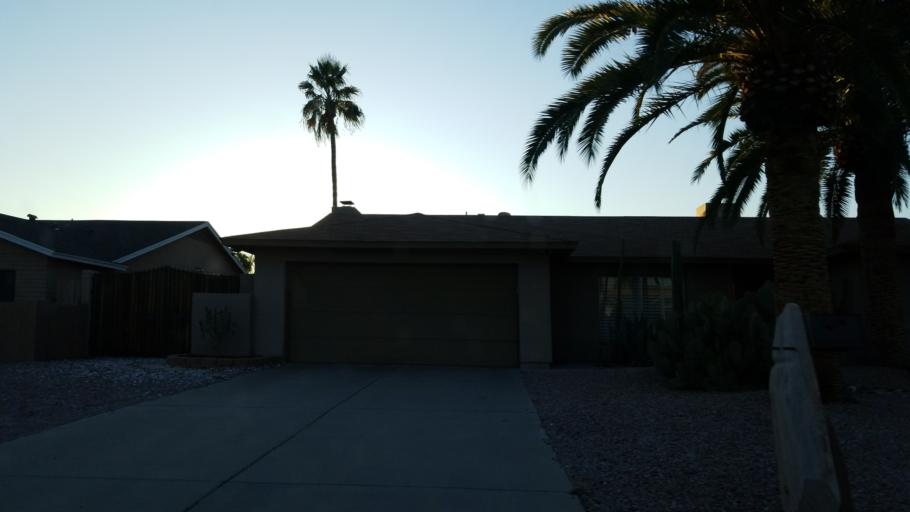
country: US
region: Arizona
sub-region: Maricopa County
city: Paradise Valley
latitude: 33.6102
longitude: -111.9736
